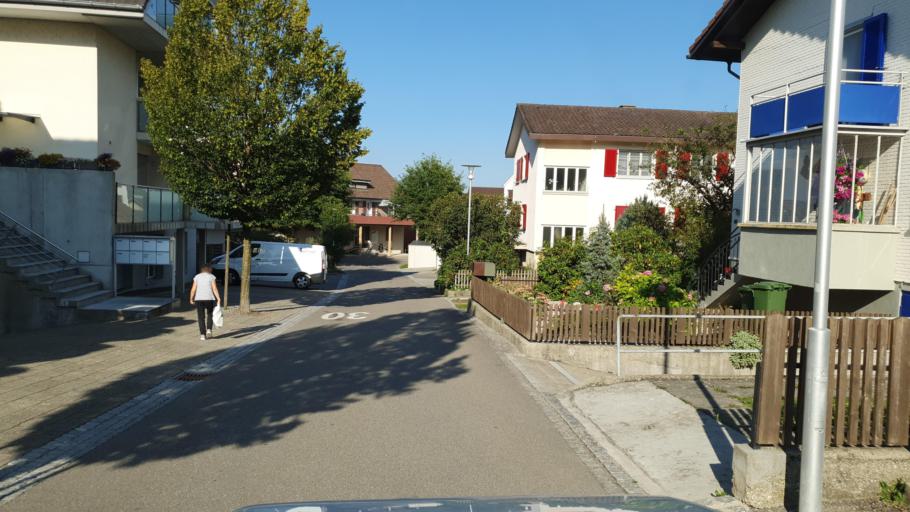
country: CH
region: Aargau
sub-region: Bezirk Muri
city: Auw
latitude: 47.2103
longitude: 8.3640
